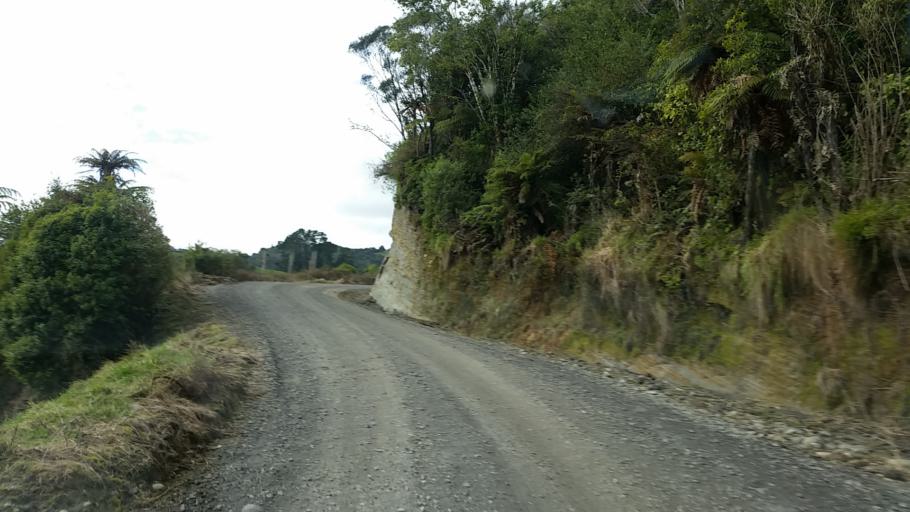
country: NZ
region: Taranaki
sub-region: New Plymouth District
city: Waitara
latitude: -39.1600
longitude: 174.5314
